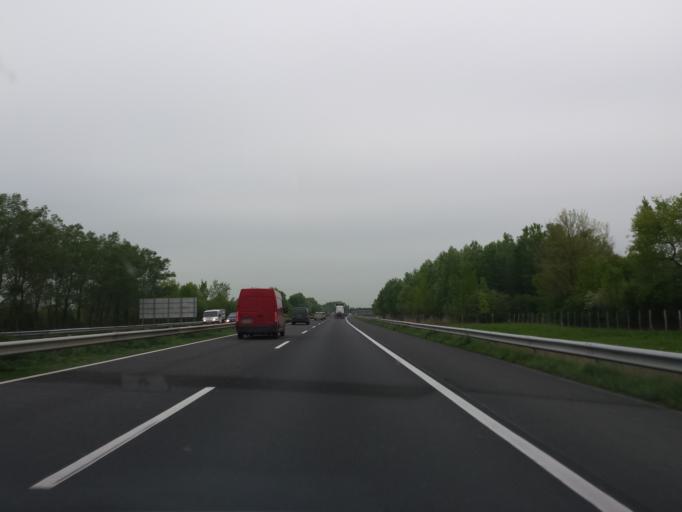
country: HU
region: Gyor-Moson-Sopron
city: Kimle
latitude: 47.7937
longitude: 17.3203
